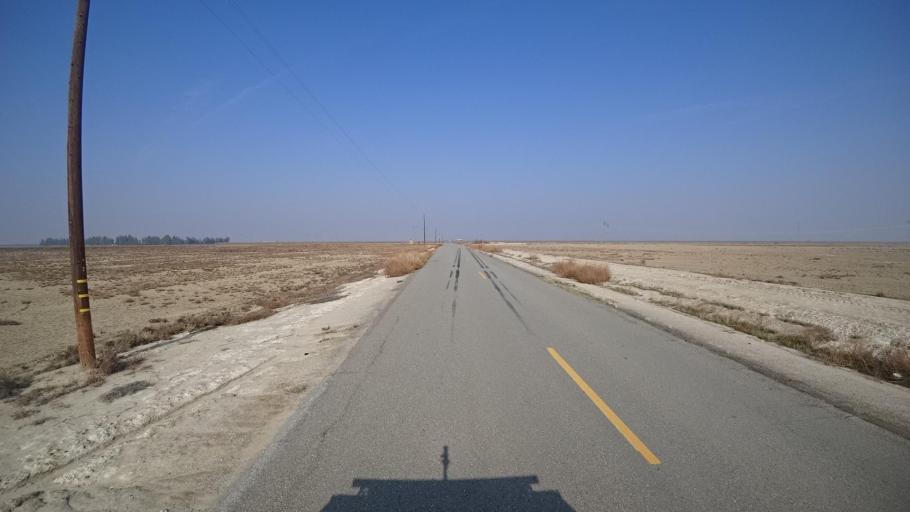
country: US
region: California
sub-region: Kern County
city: Buttonwillow
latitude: 35.3483
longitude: -119.3591
